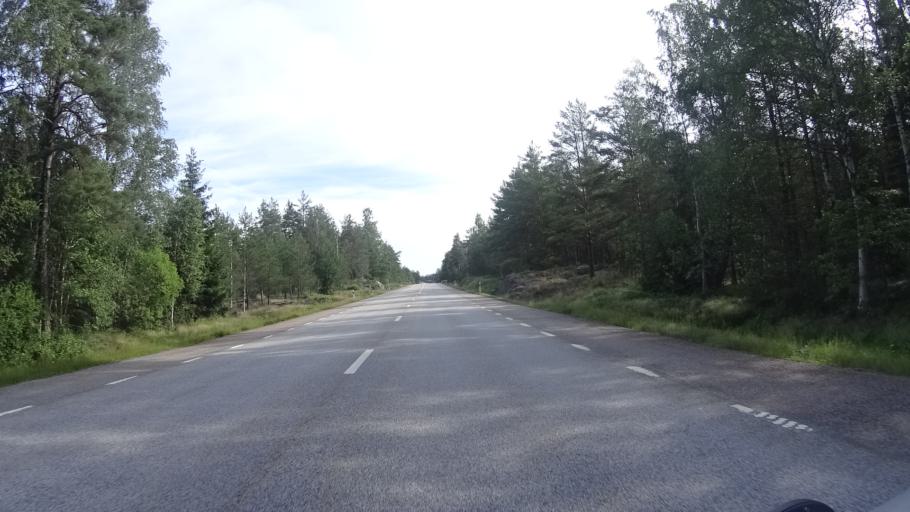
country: SE
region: Kalmar
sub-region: Oskarshamns Kommun
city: Oskarshamn
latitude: 57.4498
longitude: 16.5055
